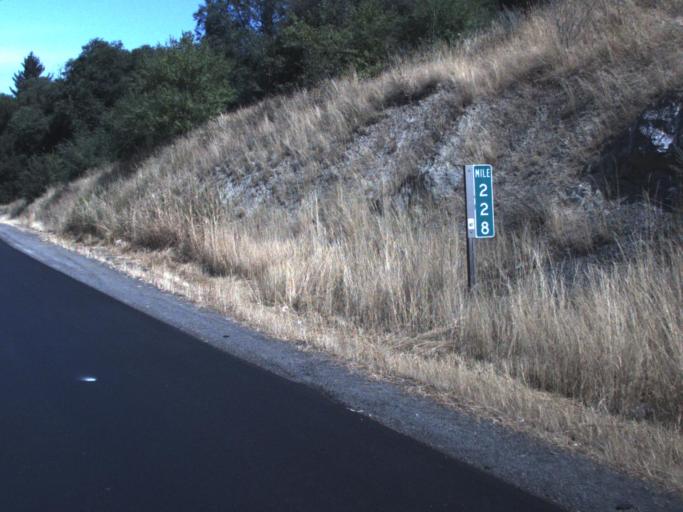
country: US
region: Washington
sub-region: Stevens County
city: Colville
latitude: 48.5234
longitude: -117.9030
